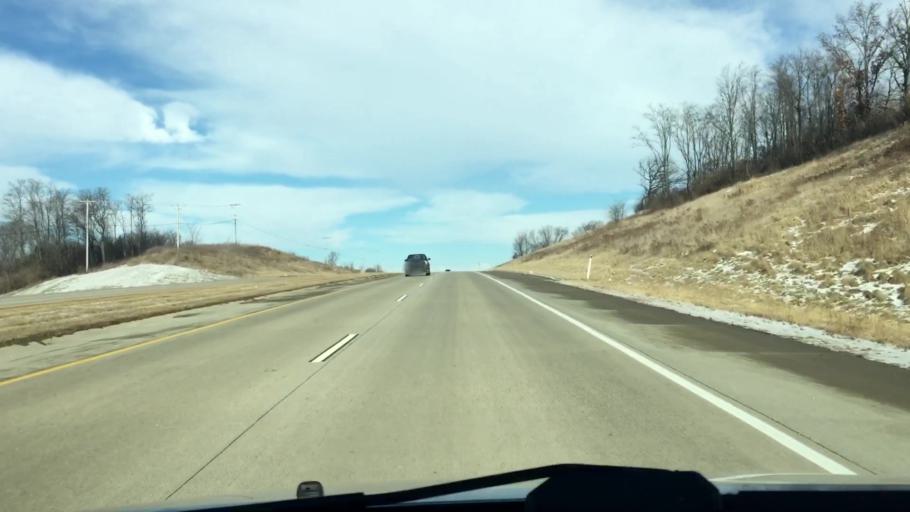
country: US
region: Wisconsin
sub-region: Waukesha County
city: Mukwonago
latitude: 42.9059
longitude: -88.3454
